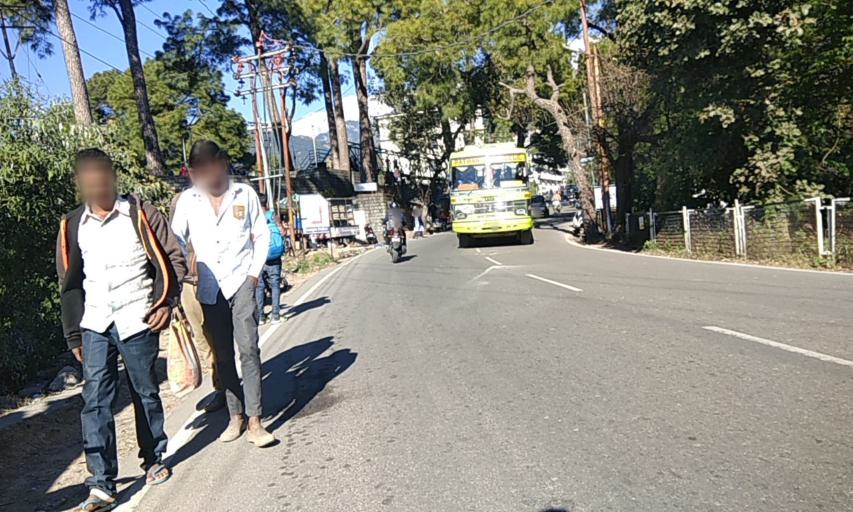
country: IN
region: Himachal Pradesh
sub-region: Kangra
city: Dharmsala
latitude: 32.2151
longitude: 76.3172
